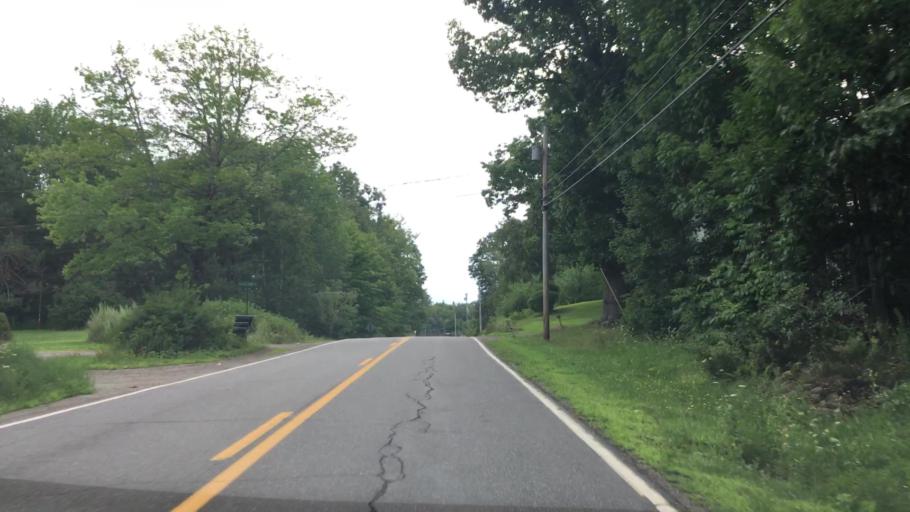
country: US
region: Maine
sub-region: Waldo County
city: Lincolnville
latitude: 44.3161
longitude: -69.0836
